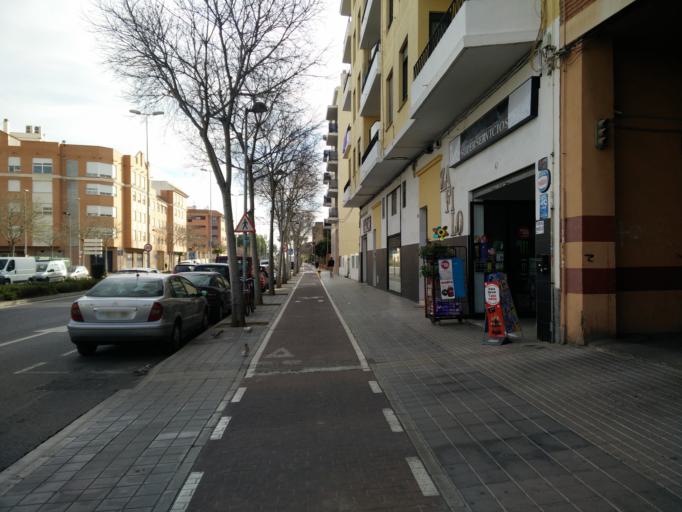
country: ES
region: Valencia
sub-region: Provincia de Castello
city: Castello de la Plana
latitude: 39.9851
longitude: -0.0498
